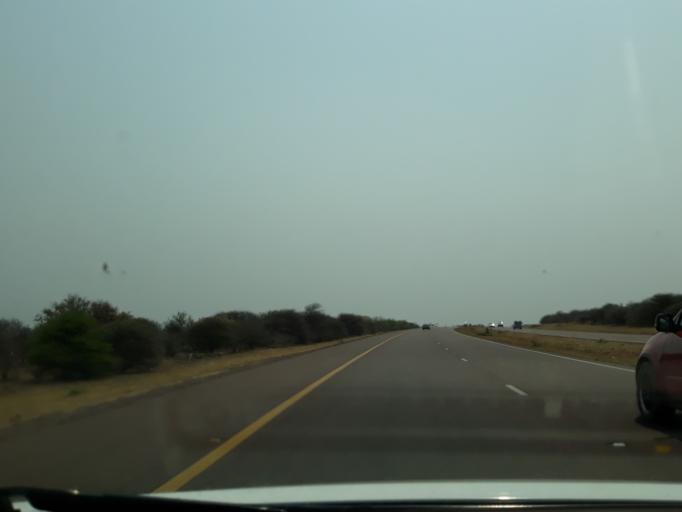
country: BW
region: Kgatleng
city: Bokaa
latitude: -24.4207
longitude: 26.0475
